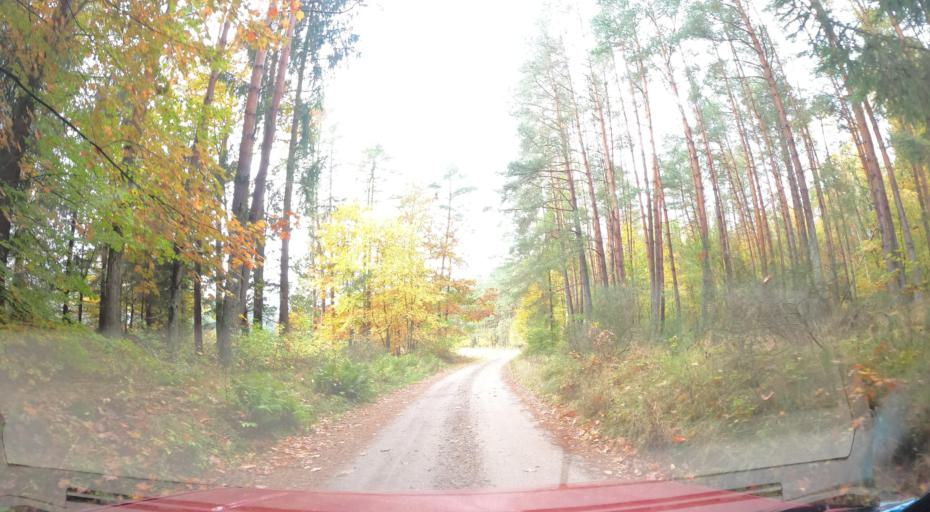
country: PL
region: West Pomeranian Voivodeship
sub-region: Powiat koszalinski
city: Sianow
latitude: 54.1523
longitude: 16.4108
